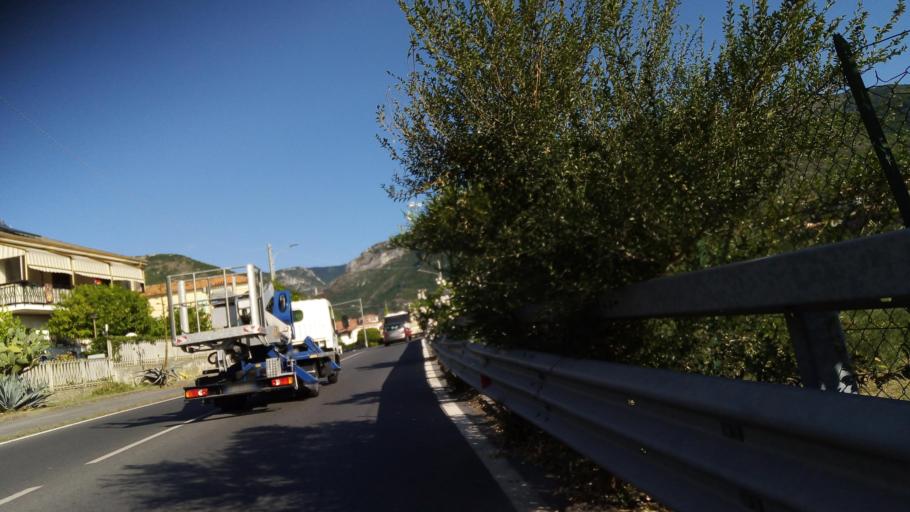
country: IT
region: Liguria
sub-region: Provincia di Savona
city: Toirano
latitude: 44.1223
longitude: 8.2145
